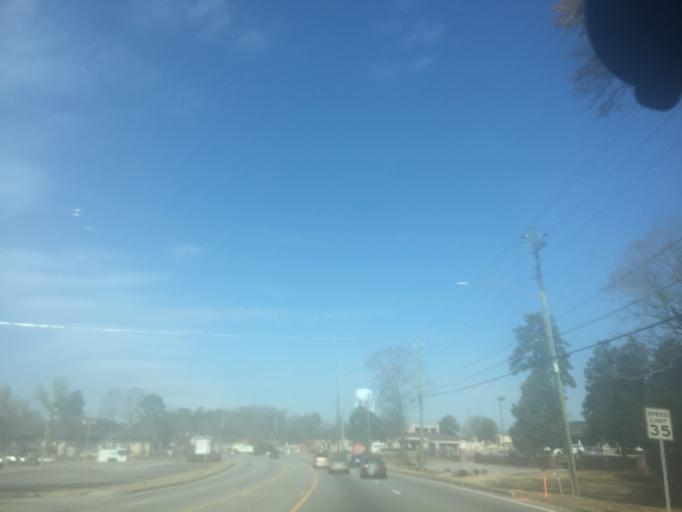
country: US
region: Georgia
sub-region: Clayton County
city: Riverdale
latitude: 33.5742
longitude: -84.4148
